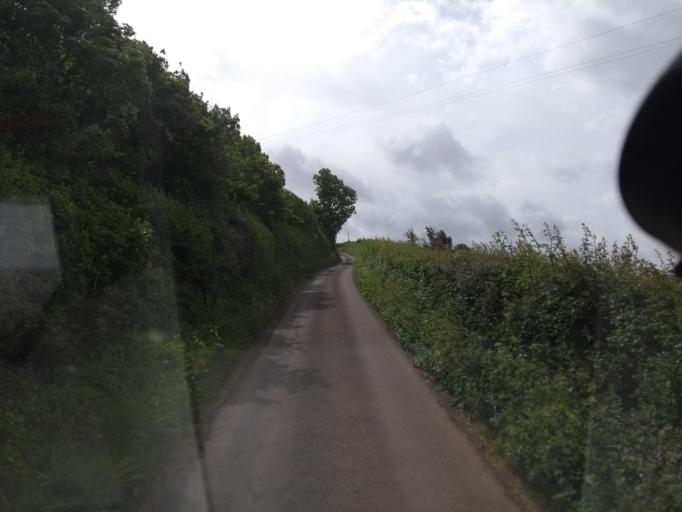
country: GB
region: England
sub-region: Somerset
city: Williton
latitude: 51.1851
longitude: -3.2155
